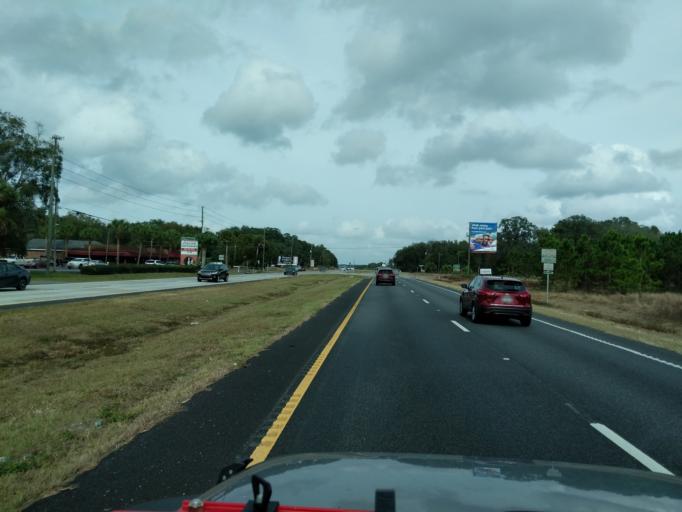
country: US
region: Florida
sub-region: Orange County
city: Tangerine
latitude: 28.7693
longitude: -81.6244
